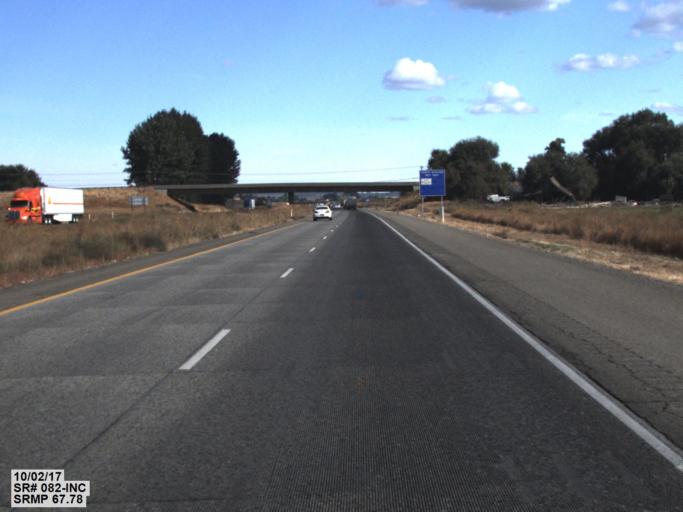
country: US
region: Washington
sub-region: Yakima County
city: Sunnyside
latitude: 46.3058
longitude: -120.0026
